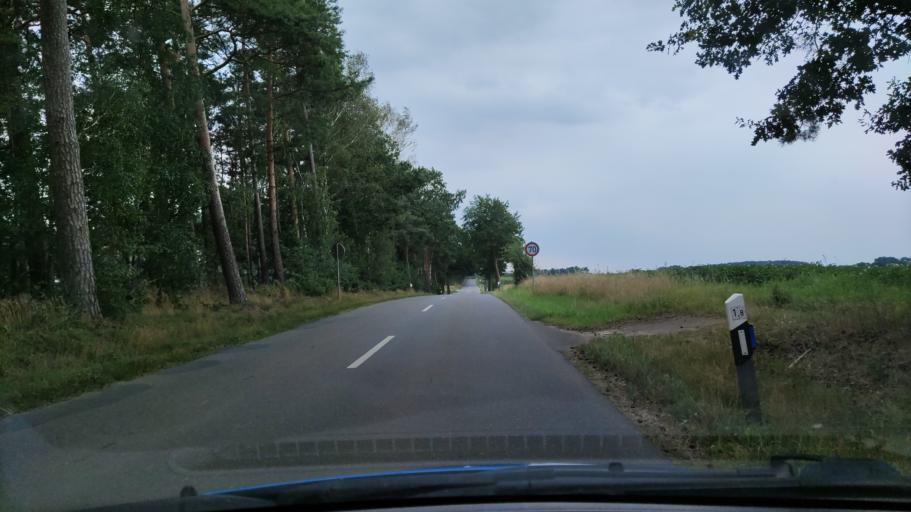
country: DE
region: Lower Saxony
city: Rosche
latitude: 53.0144
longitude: 10.7661
